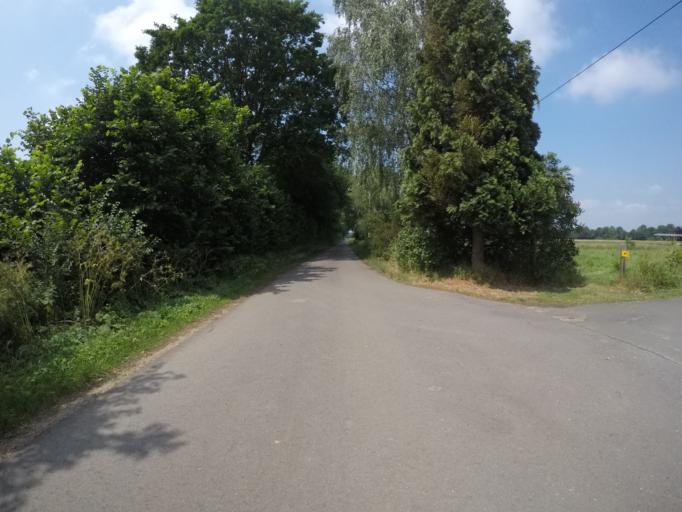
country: DE
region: North Rhine-Westphalia
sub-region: Regierungsbezirk Munster
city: Isselburg
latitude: 51.8463
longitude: 6.5305
